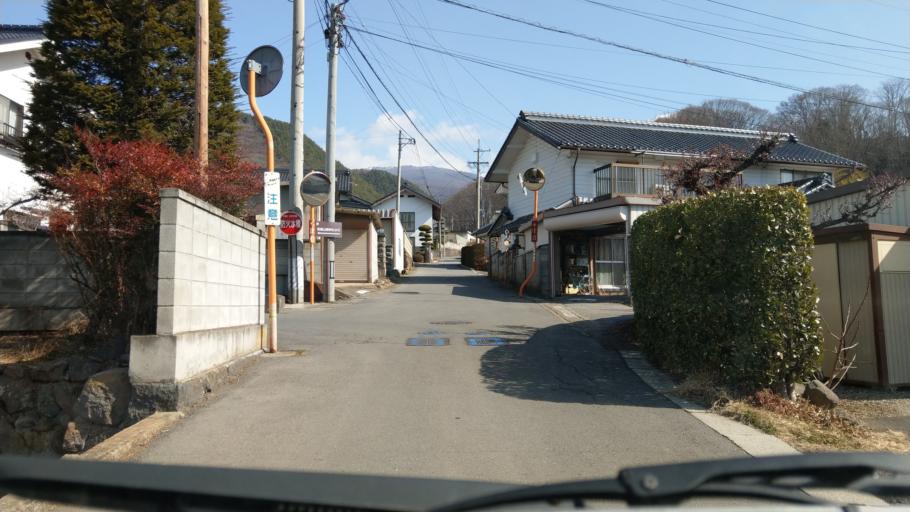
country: JP
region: Nagano
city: Ueda
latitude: 36.3772
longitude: 138.3532
